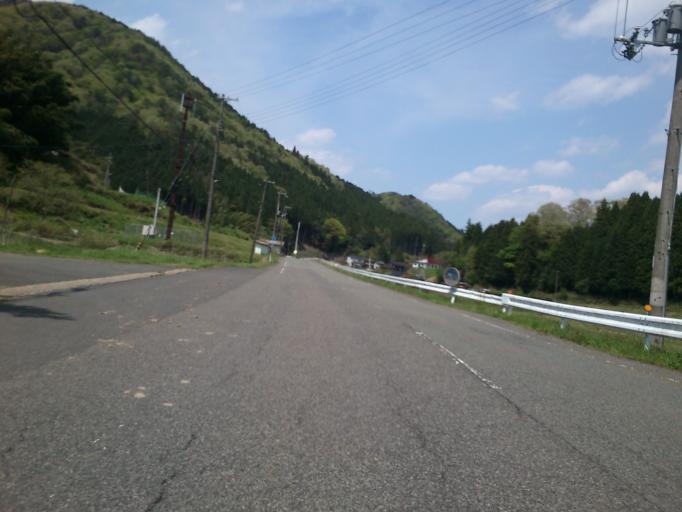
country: JP
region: Hyogo
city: Toyooka
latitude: 35.3875
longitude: 134.9404
